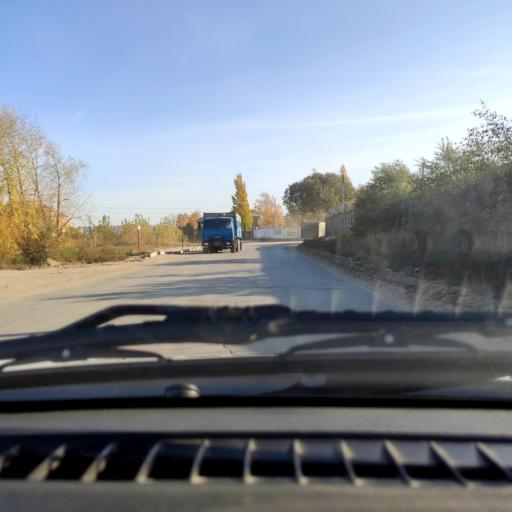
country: RU
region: Samara
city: Zhigulevsk
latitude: 53.4762
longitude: 49.4981
